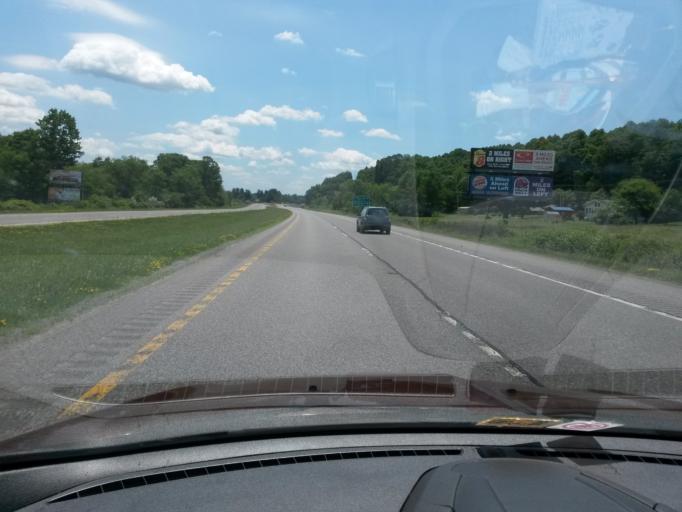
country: US
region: West Virginia
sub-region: Nicholas County
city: Summersville
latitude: 38.3372
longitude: -80.8353
